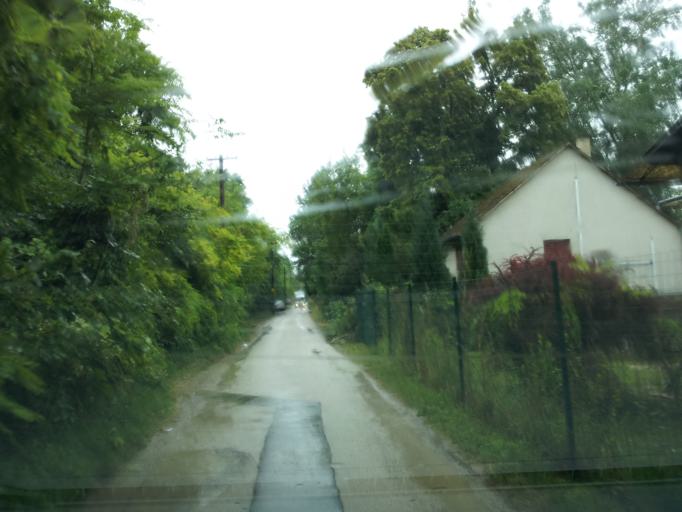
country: HU
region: Veszprem
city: Balatonkenese
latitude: 47.0173
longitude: 18.1497
